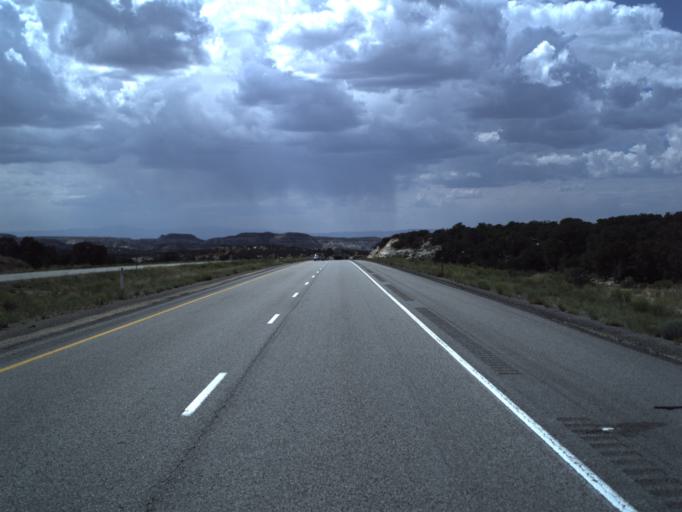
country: US
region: Utah
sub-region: Emery County
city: Ferron
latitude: 38.8594
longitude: -110.8268
